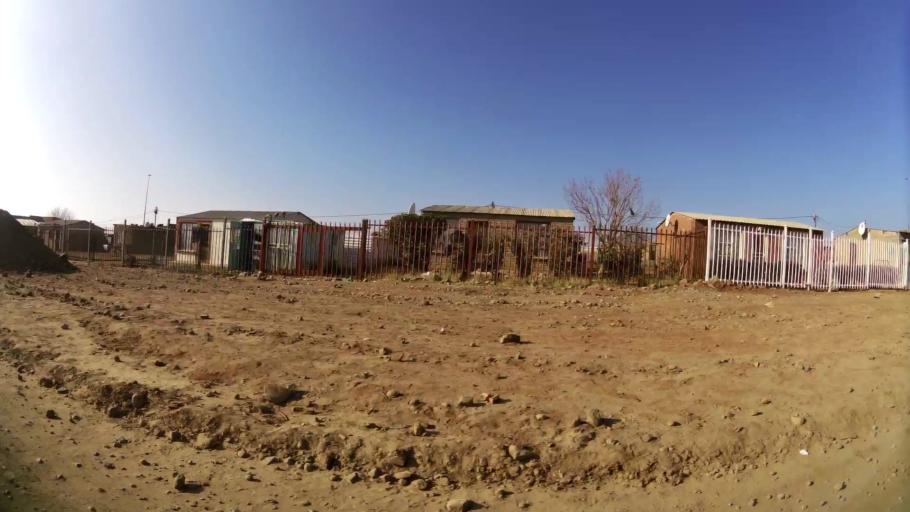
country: ZA
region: Orange Free State
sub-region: Mangaung Metropolitan Municipality
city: Bloemfontein
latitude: -29.2014
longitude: 26.2547
